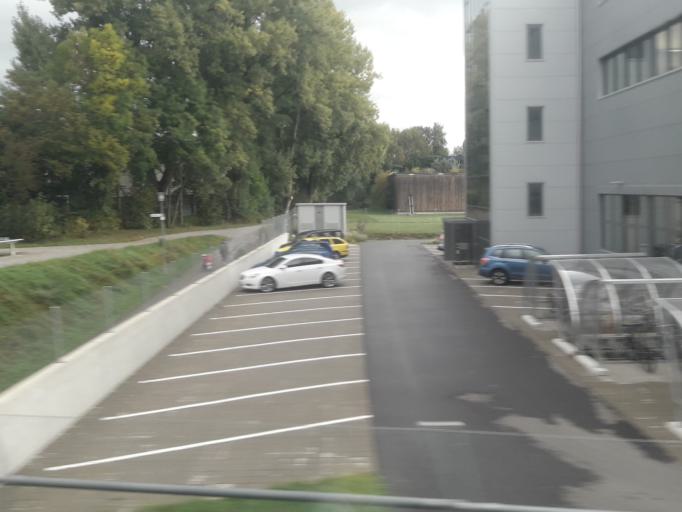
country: CH
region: Bern
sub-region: Thun District
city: Uetendorf
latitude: 46.7739
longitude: 7.5835
